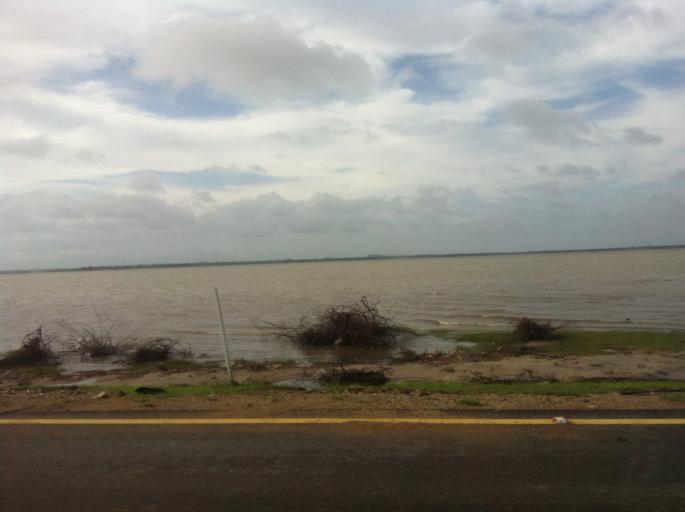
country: IN
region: Tamil Nadu
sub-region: Kancheepuram
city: Cheyyur
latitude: 12.3468
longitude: 80.0534
